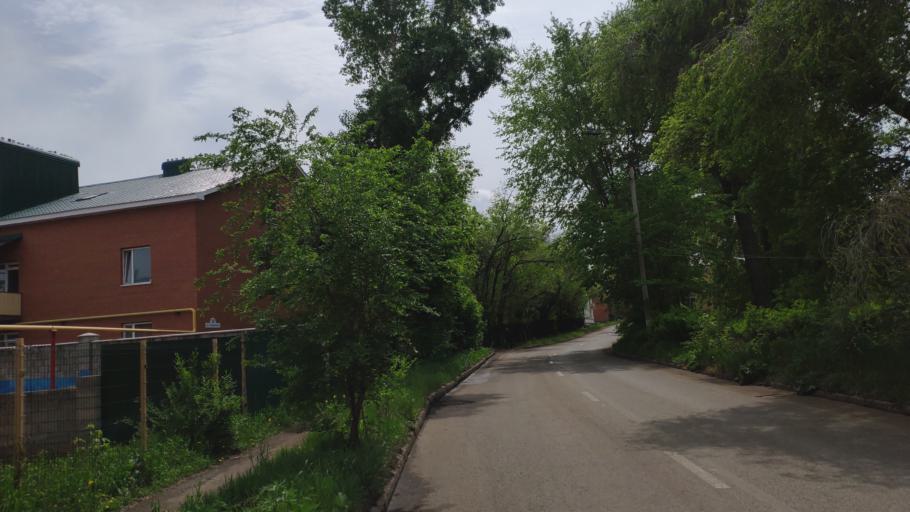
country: RU
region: Chelyabinsk
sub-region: Gorod Magnitogorsk
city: Magnitogorsk
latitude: 53.4205
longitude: 58.9564
